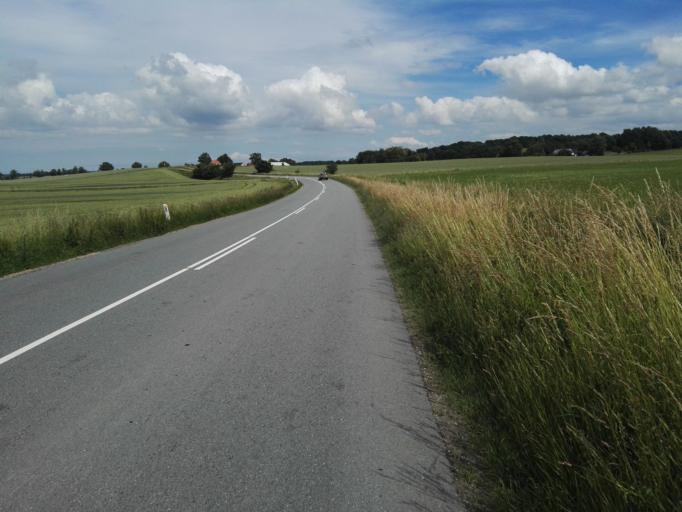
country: DK
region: Capital Region
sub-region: Frederikssund Kommune
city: Slangerup
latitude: 55.8603
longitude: 12.1766
